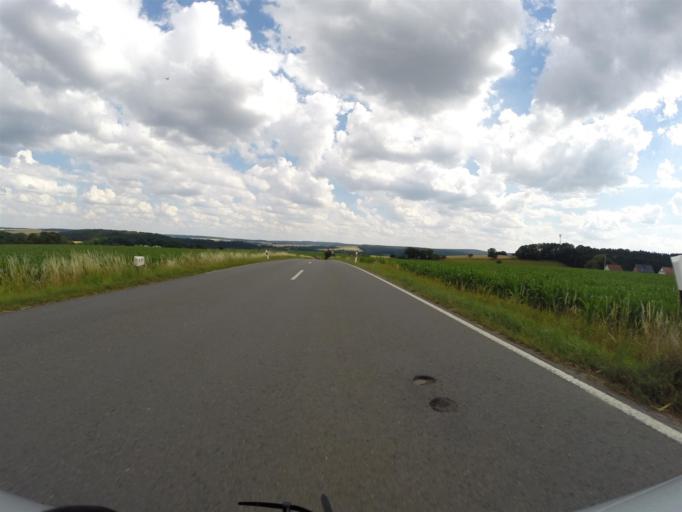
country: DE
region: Thuringia
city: Schloben
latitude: 50.8885
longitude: 11.6899
